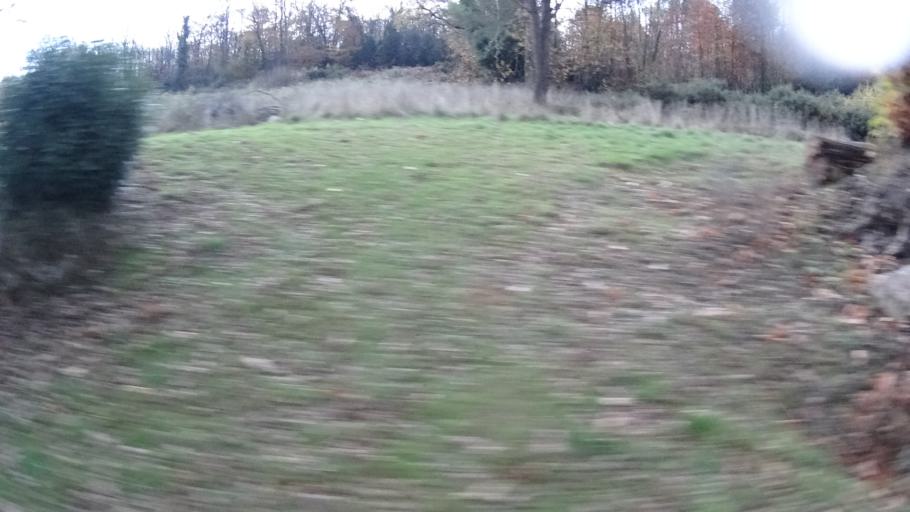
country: FR
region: Pays de la Loire
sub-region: Departement de la Loire-Atlantique
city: Avessac
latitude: 47.6624
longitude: -2.0160
